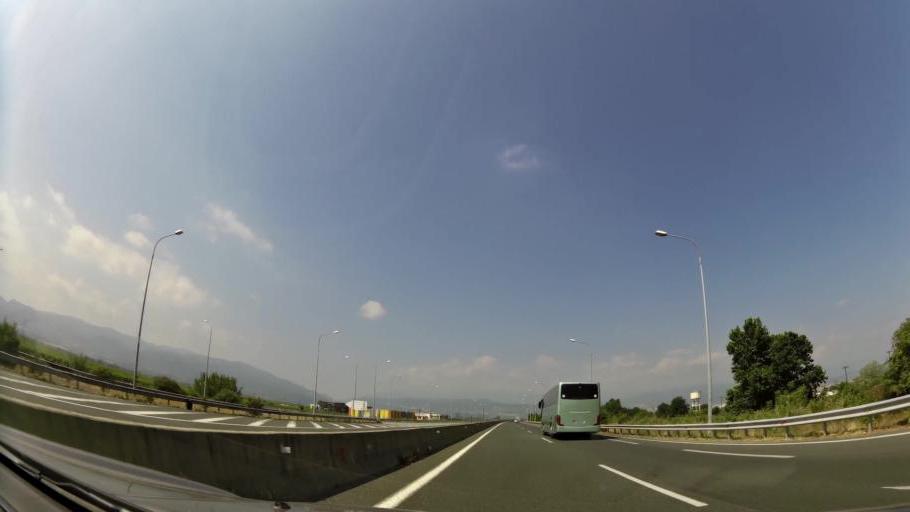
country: GR
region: Central Macedonia
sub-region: Nomos Imathias
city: Kouloura
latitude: 40.5400
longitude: 22.3141
